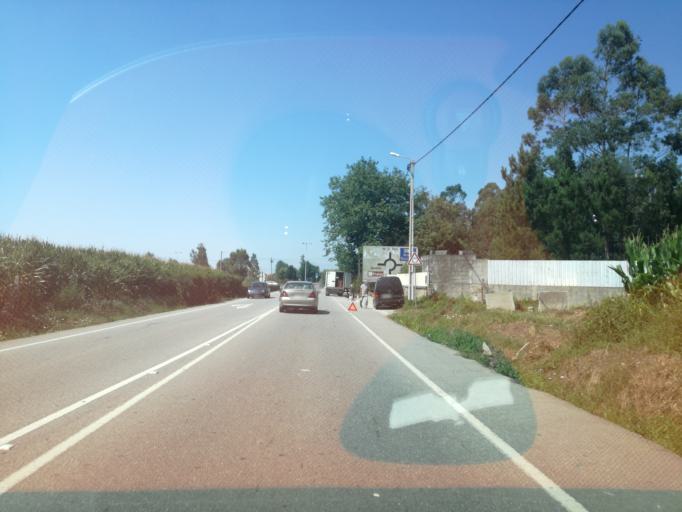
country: PT
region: Braga
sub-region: Esposende
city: Apulia
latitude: 41.4821
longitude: -8.7490
